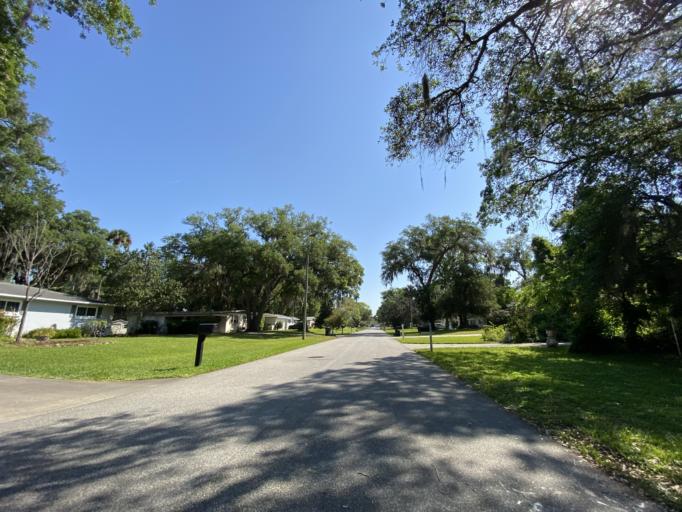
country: US
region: Florida
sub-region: Volusia County
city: South Daytona
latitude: 29.1629
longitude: -81.0142
